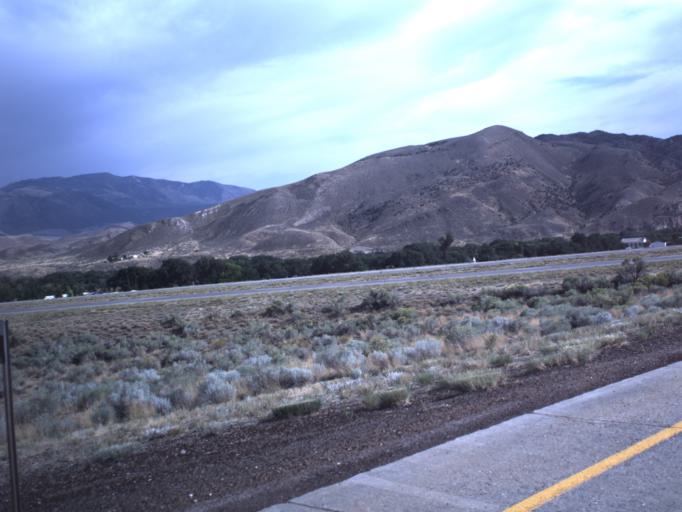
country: US
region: Utah
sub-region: Sevier County
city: Monroe
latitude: 38.6013
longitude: -112.2518
